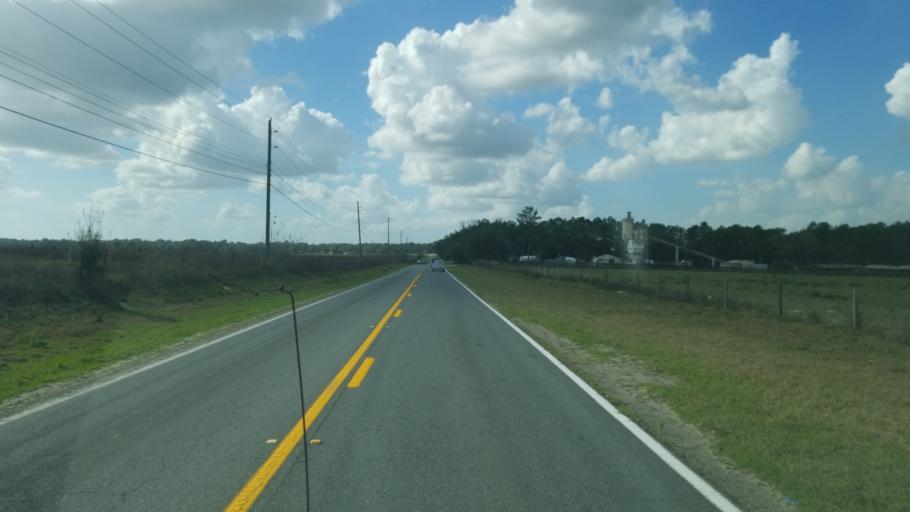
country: US
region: Florida
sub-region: Marion County
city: Ocala
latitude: 29.1502
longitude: -82.2372
